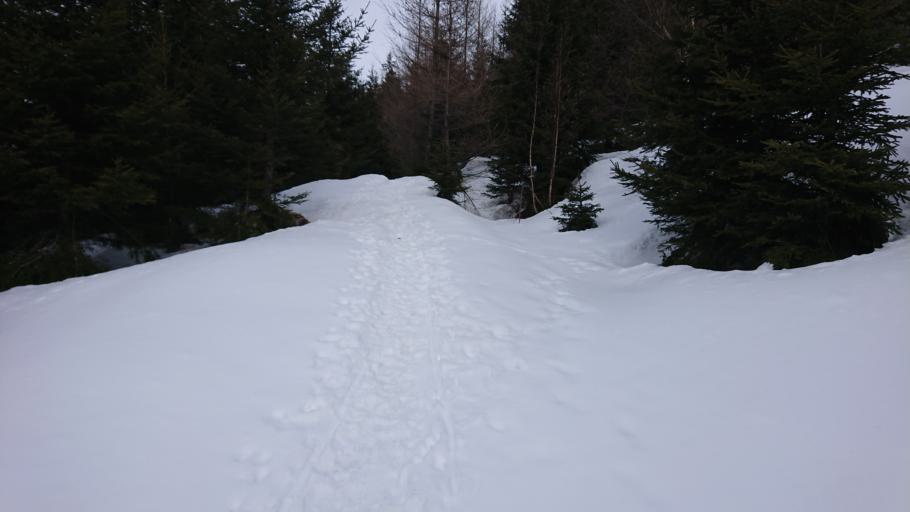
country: IT
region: Trentino-Alto Adige
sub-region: Bolzano
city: Prati
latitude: 46.9157
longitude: 11.4675
